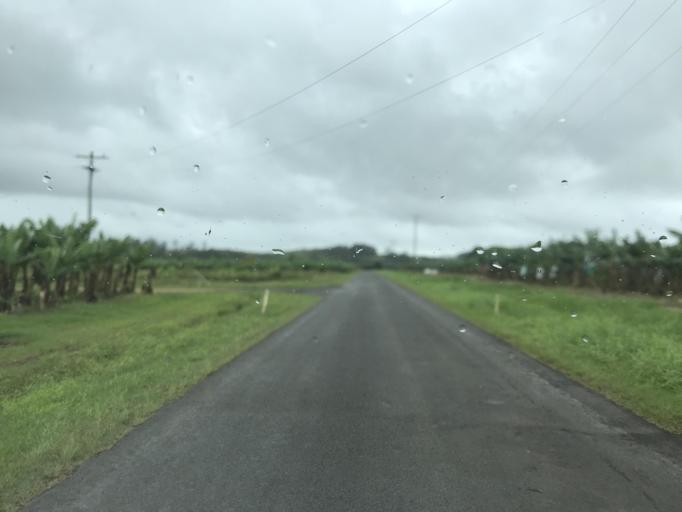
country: AU
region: Queensland
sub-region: Cassowary Coast
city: Innisfail
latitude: -17.5084
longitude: 145.9790
